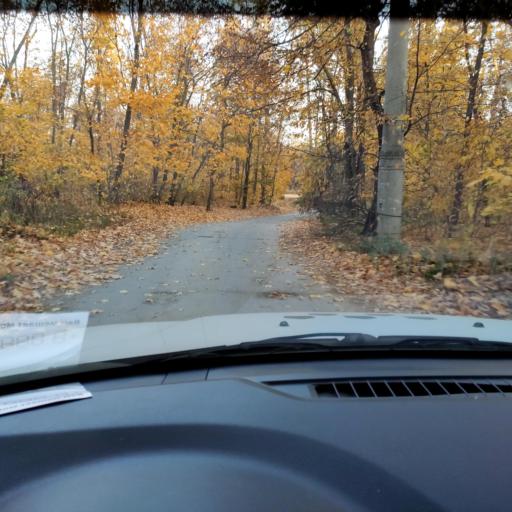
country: RU
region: Samara
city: Tol'yatti
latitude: 53.4915
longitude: 49.3013
